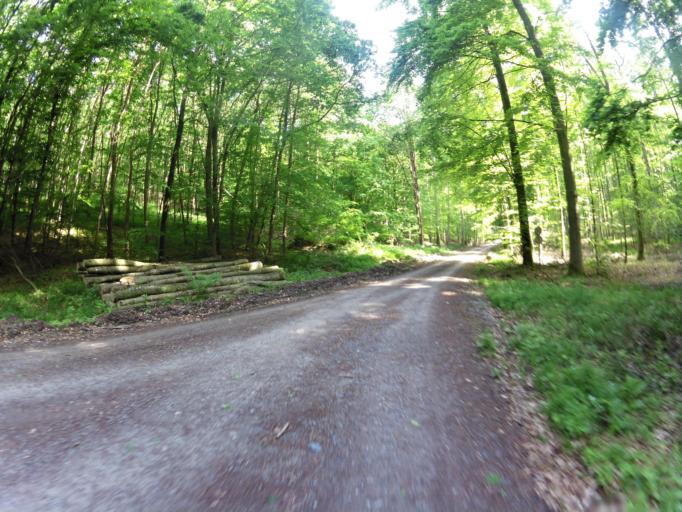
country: DE
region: Bavaria
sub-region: Regierungsbezirk Unterfranken
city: Uettingen
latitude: 49.7789
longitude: 9.7415
